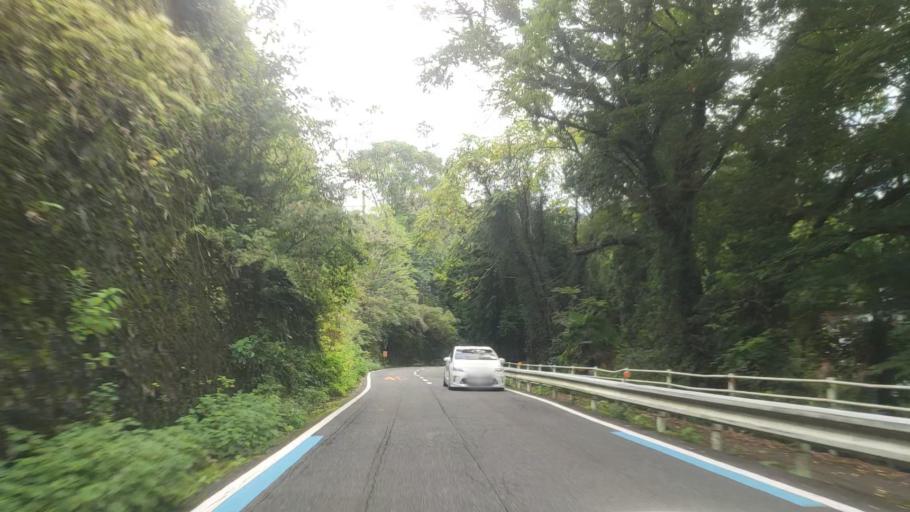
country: JP
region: Wakayama
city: Hashimoto
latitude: 34.2862
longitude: 135.5626
